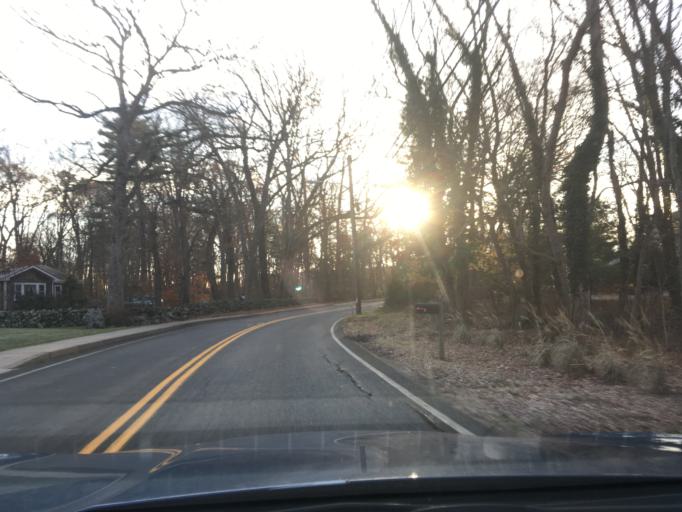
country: US
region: Rhode Island
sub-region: Washington County
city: North Kingstown
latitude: 41.5575
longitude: -71.4528
